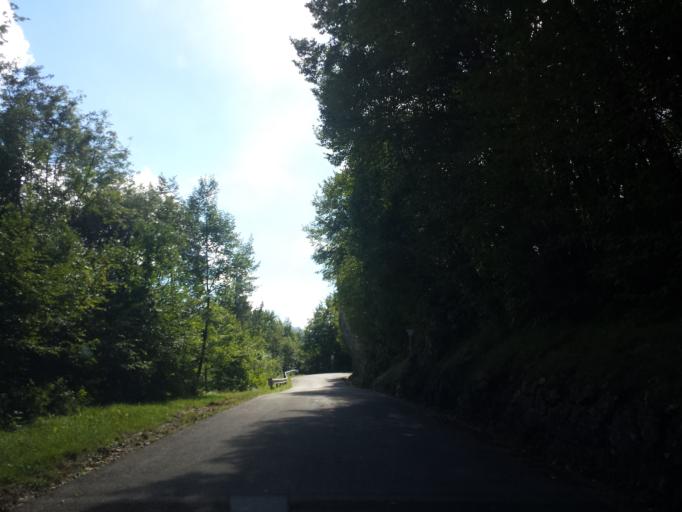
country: IT
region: Veneto
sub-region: Provincia di Vicenza
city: Recoaro Terme
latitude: 45.7178
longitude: 11.1937
